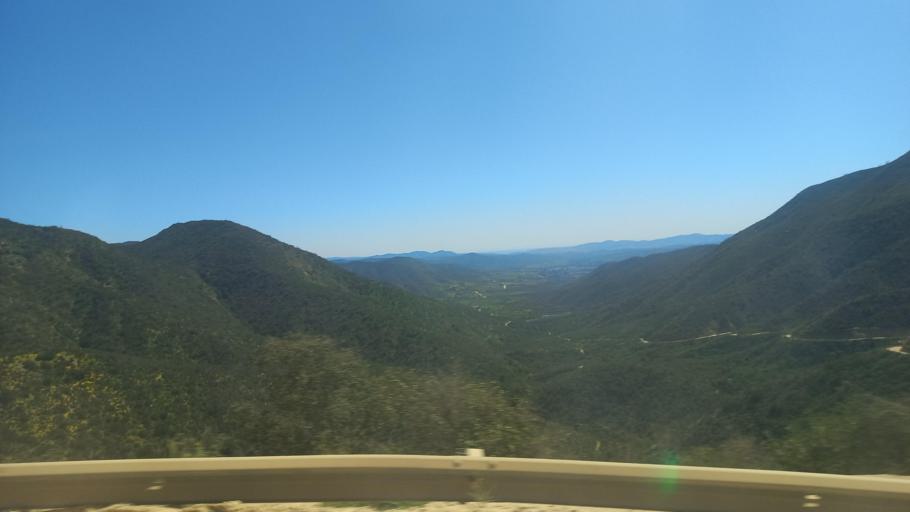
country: CL
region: Valparaiso
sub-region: Provincia de Marga Marga
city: Limache
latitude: -33.2071
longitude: -71.2588
